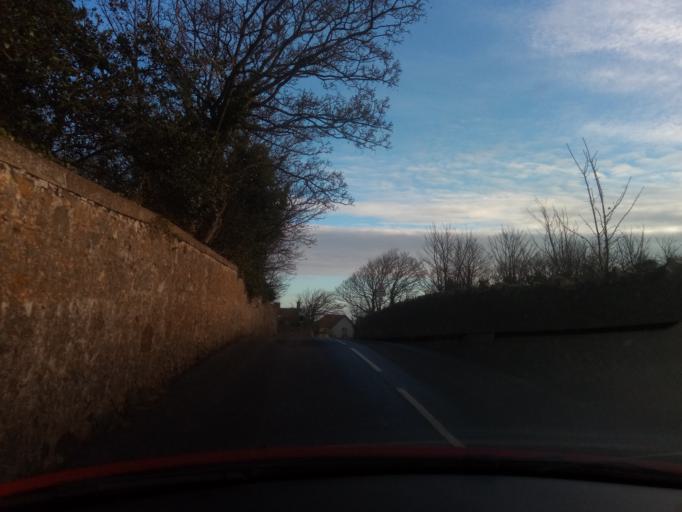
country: GB
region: Scotland
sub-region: The Scottish Borders
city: Eyemouth
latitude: 55.8999
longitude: -2.1345
